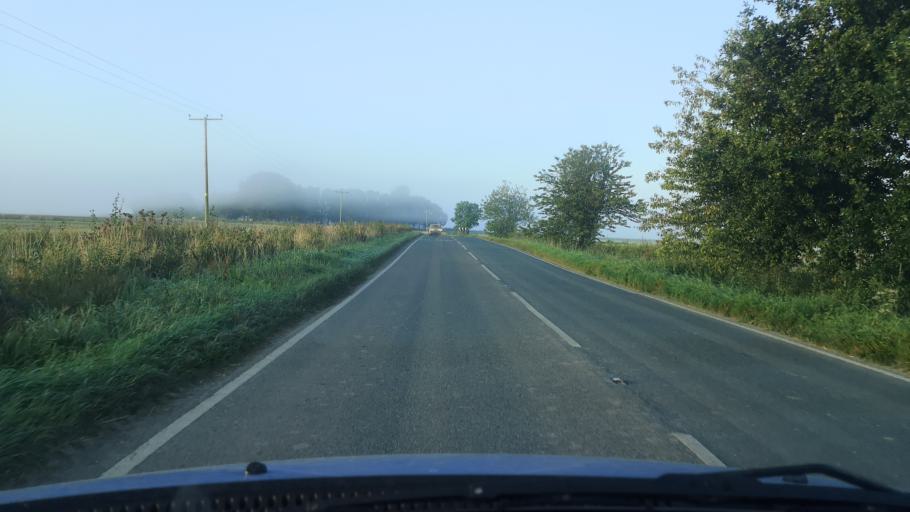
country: GB
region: England
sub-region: North Lincolnshire
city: Eastoft
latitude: 53.6696
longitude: -0.7714
